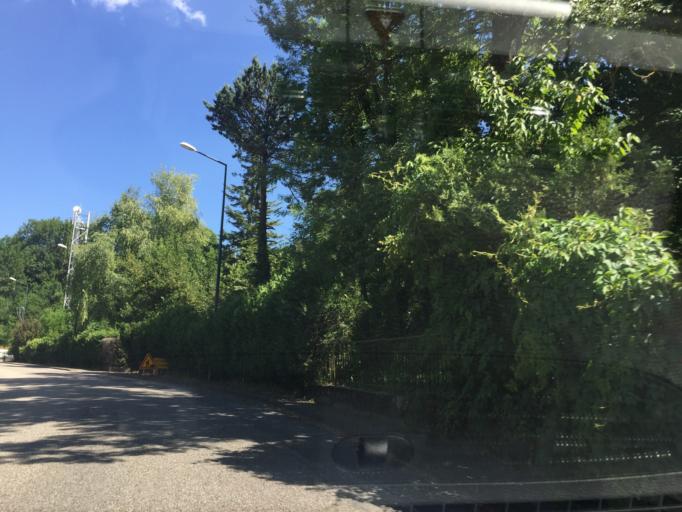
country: FR
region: Rhone-Alpes
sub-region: Departement de l'Isere
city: Saint-Just-de-Claix
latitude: 45.0584
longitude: 5.2508
